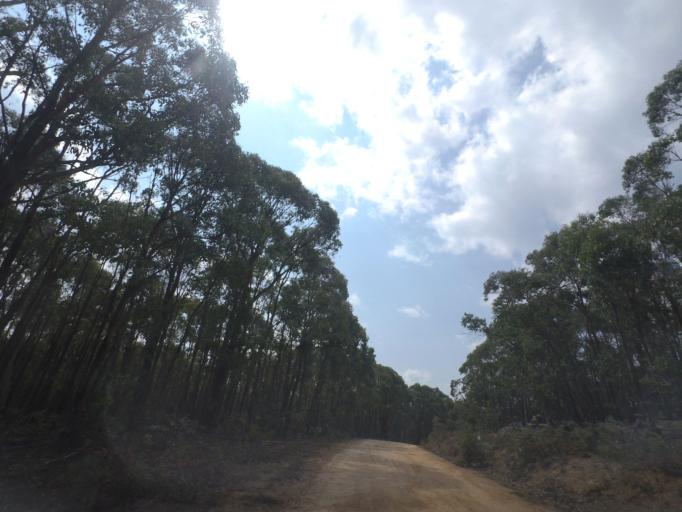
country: AU
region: Victoria
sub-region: Moorabool
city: Bacchus Marsh
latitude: -37.4699
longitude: 144.3916
